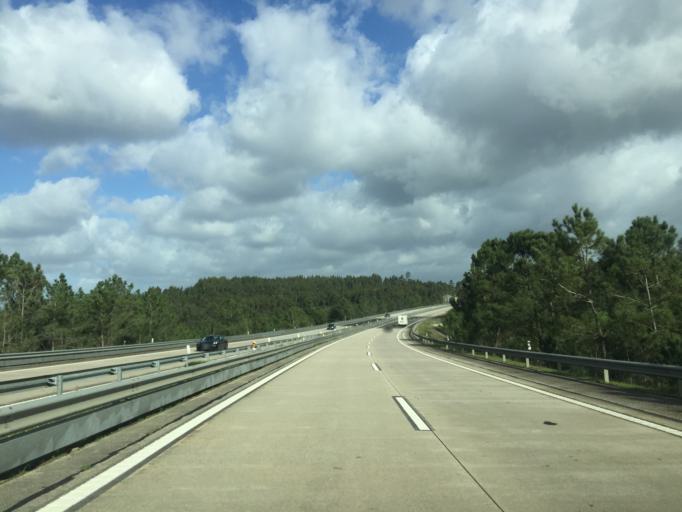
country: PT
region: Lisbon
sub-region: Torres Vedras
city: Torres Vedras
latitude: 39.1387
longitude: -9.2482
